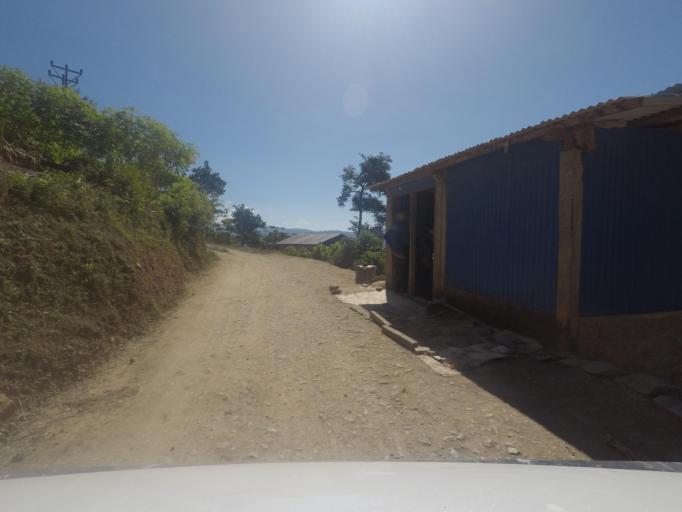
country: TL
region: Ermera
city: Gleno
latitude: -8.7253
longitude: 125.3324
